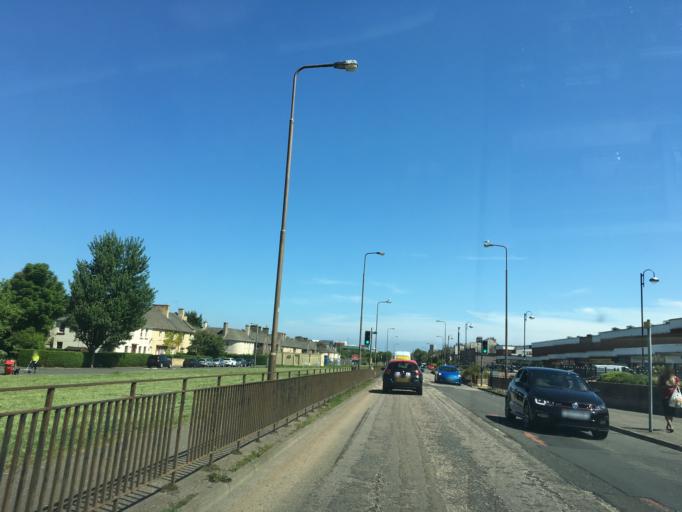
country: GB
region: Scotland
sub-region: Edinburgh
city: Edinburgh
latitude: 55.9673
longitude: -3.2469
